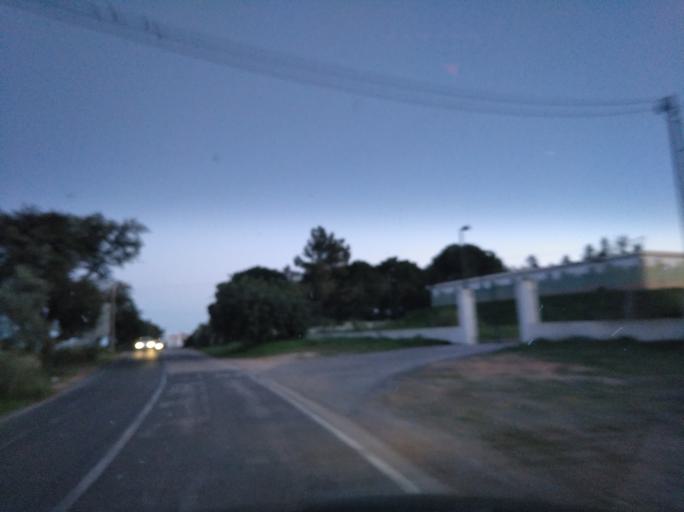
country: PT
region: Faro
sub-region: Vila Real de Santo Antonio
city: Monte Gordo
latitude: 37.1909
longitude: -7.5131
